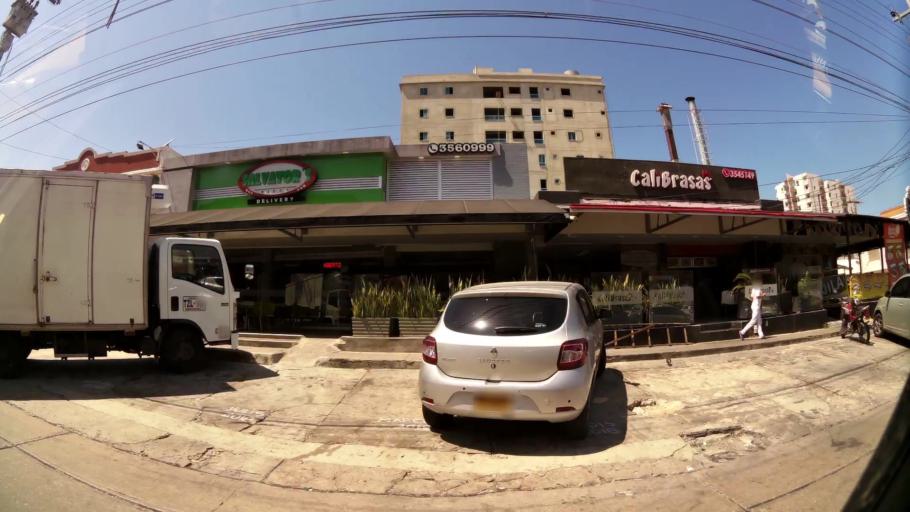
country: CO
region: Atlantico
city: Barranquilla
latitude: 10.9998
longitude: -74.8197
